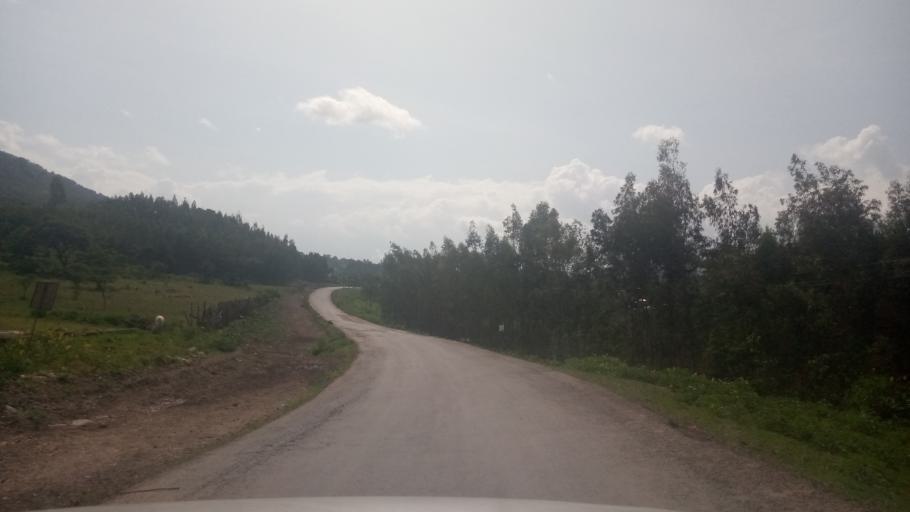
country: ET
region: Oromiya
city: Agaro
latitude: 7.9957
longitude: 36.5036
